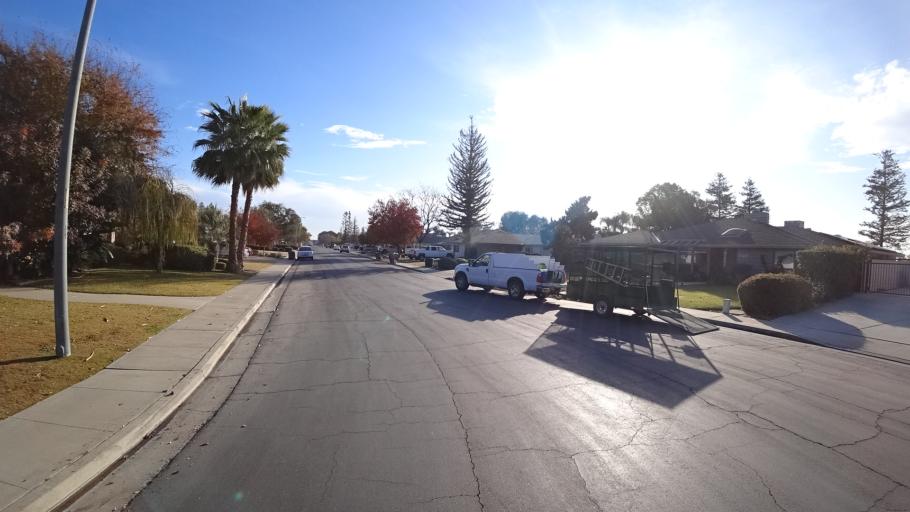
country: US
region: California
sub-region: Kern County
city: Rosedale
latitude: 35.3478
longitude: -119.1525
